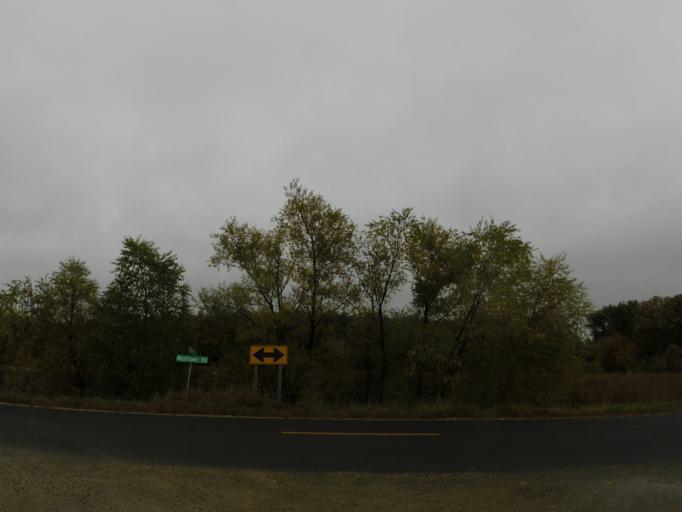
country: US
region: Minnesota
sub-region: Scott County
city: Prior Lake
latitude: 44.6854
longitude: -93.4196
